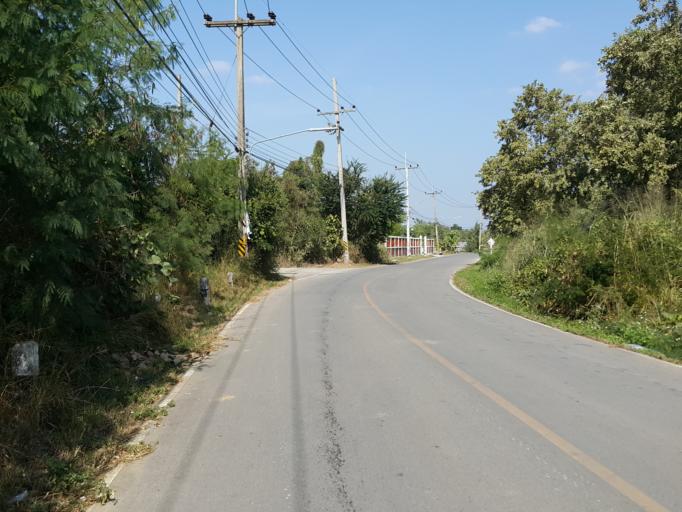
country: TH
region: Chiang Mai
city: San Kamphaeng
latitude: 18.7878
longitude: 99.1266
